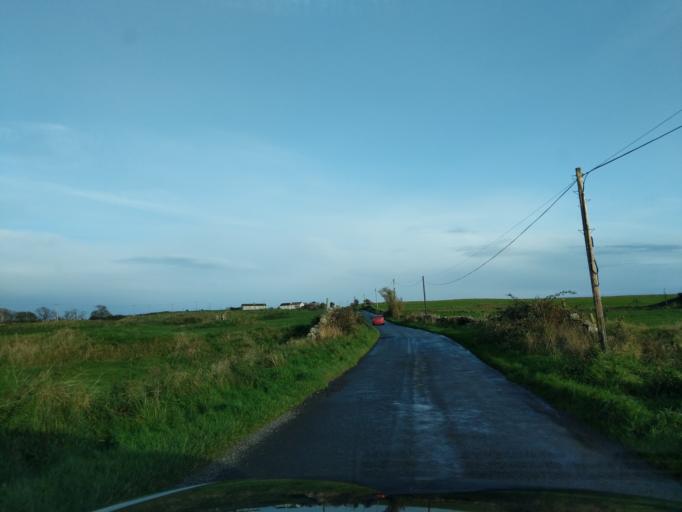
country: GB
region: Scotland
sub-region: Dumfries and Galloway
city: Kirkcudbright
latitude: 54.8125
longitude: -4.1556
